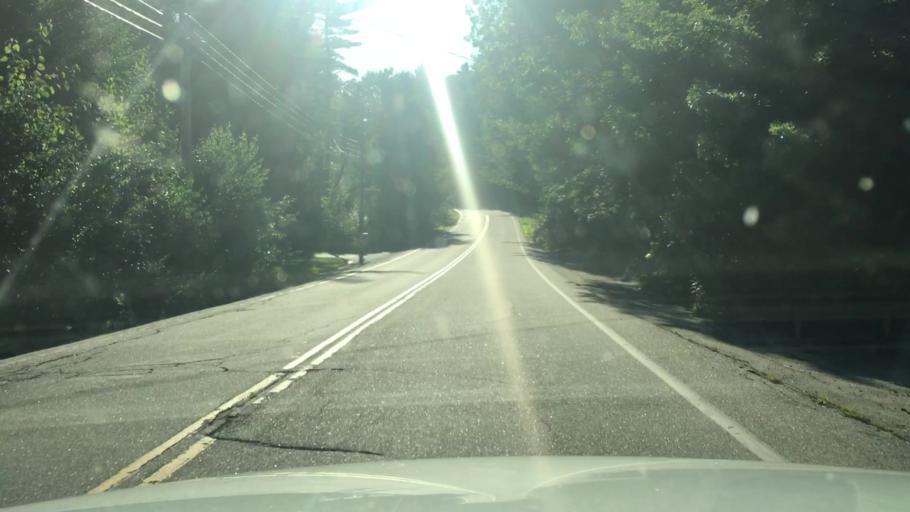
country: US
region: New Hampshire
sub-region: Rockingham County
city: Sandown
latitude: 42.9212
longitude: -71.1725
